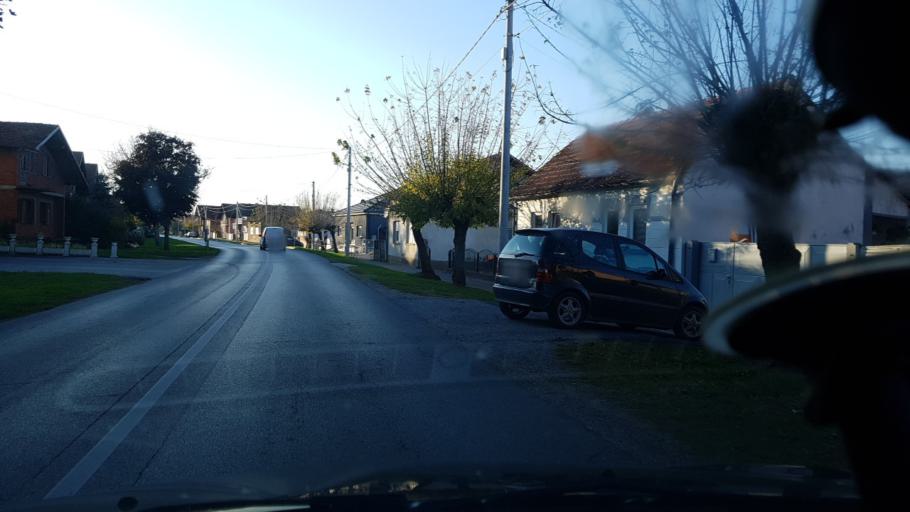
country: HR
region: Koprivnicko-Krizevacka
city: Virje
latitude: 46.0469
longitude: 17.0522
